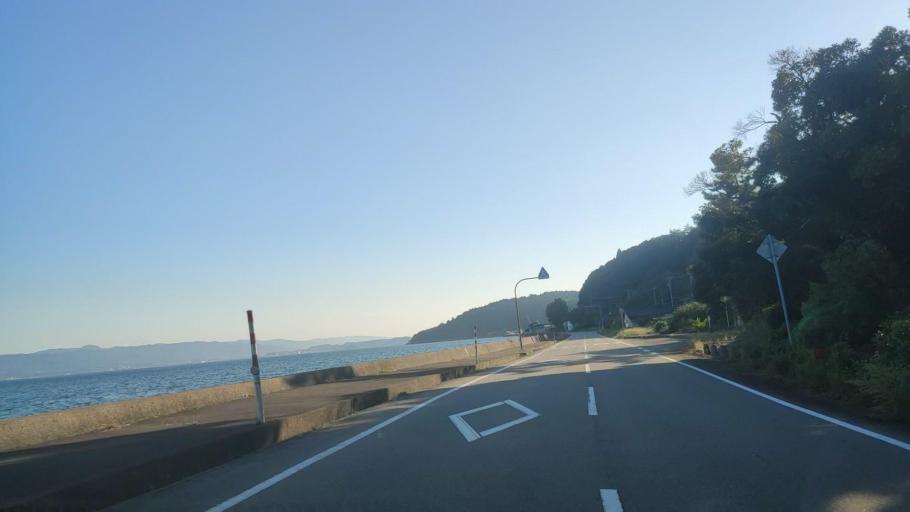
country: JP
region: Ishikawa
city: Nanao
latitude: 37.1116
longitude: 136.9859
